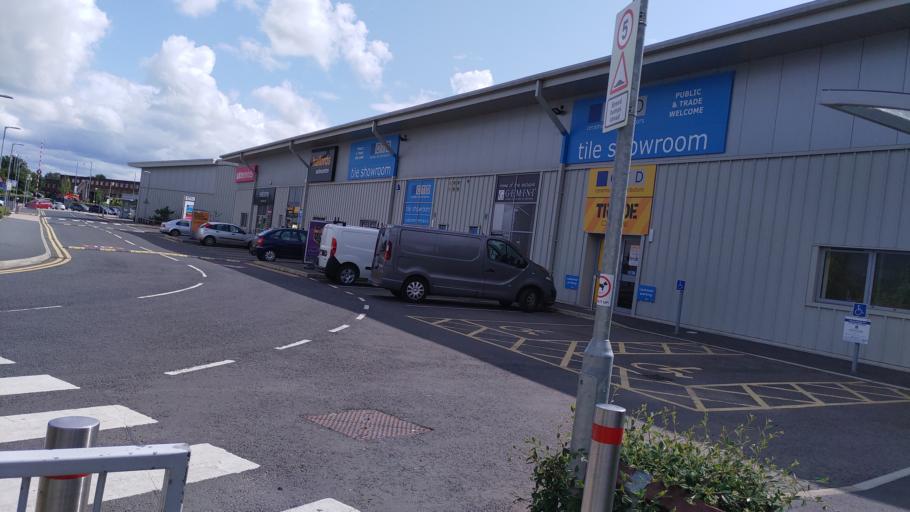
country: GB
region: England
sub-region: Lancashire
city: Preston
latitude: 53.7743
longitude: -2.6808
